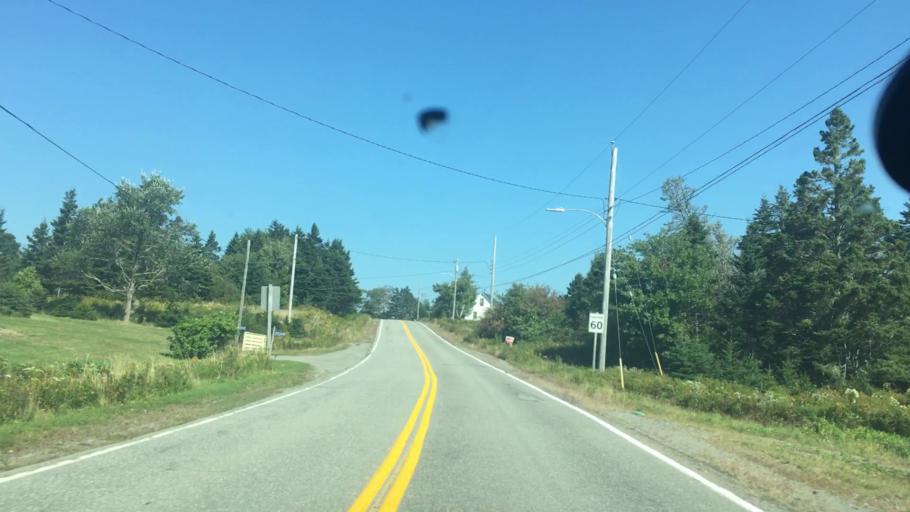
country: CA
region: Nova Scotia
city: New Glasgow
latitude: 44.9120
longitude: -62.3843
